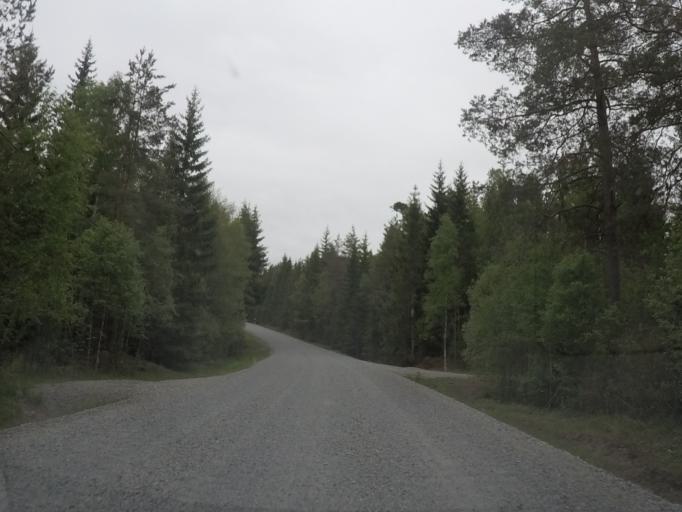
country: SE
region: Soedermanland
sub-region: Flens Kommun
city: Halleforsnas
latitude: 59.1831
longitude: 16.4988
